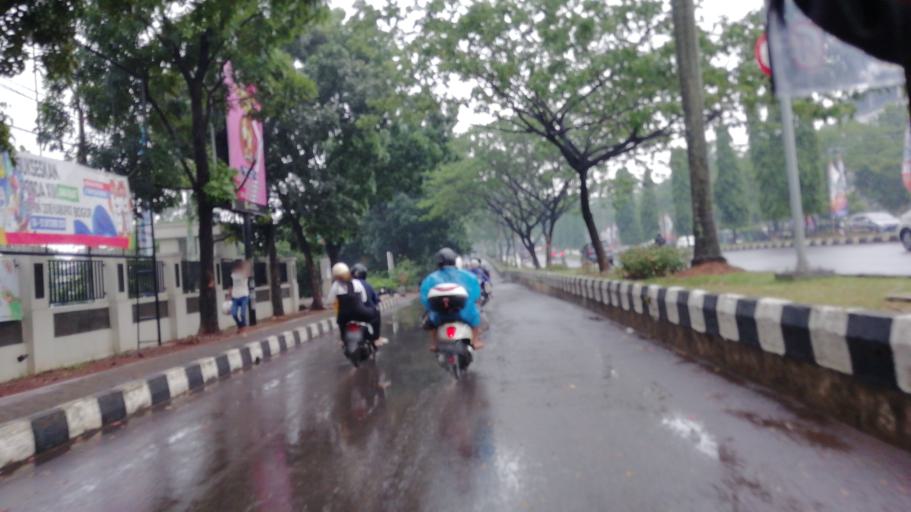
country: ID
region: West Java
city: Cibinong
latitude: -6.4829
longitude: 106.8324
